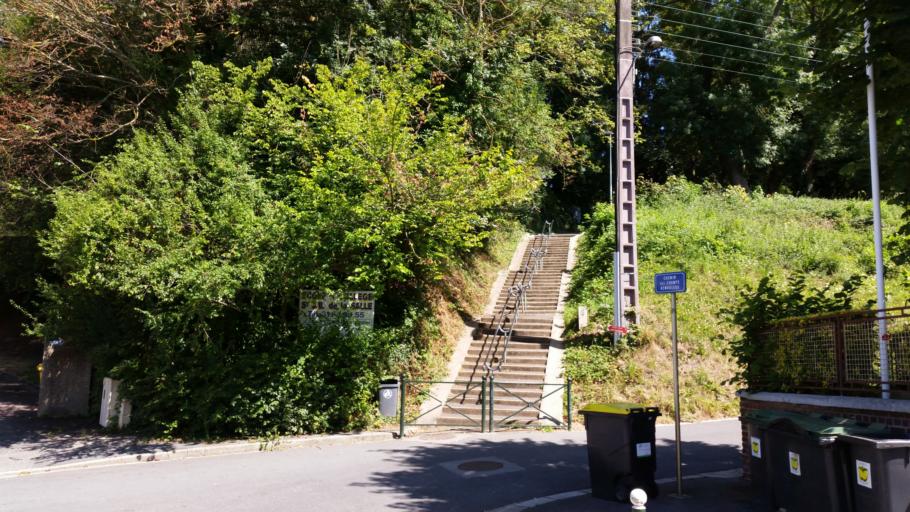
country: FR
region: Lower Normandy
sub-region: Departement du Calvados
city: Lisieux
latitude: 49.1422
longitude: 0.2319
